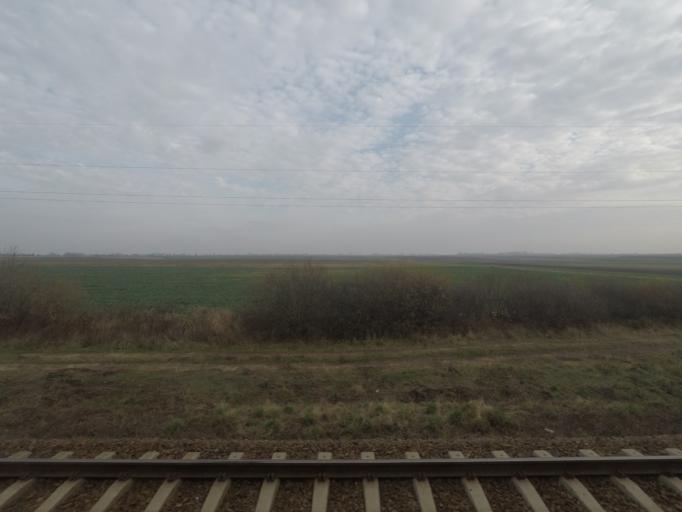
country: PL
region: Subcarpathian Voivodeship
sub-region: Powiat jaroslawski
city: Sosnica
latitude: 49.8579
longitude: 22.8545
